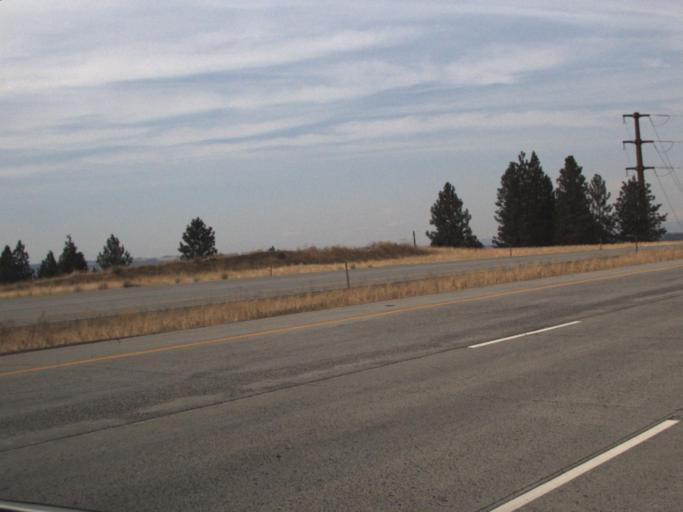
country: US
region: Washington
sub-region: Spokane County
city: Mead
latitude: 47.7403
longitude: -117.3606
